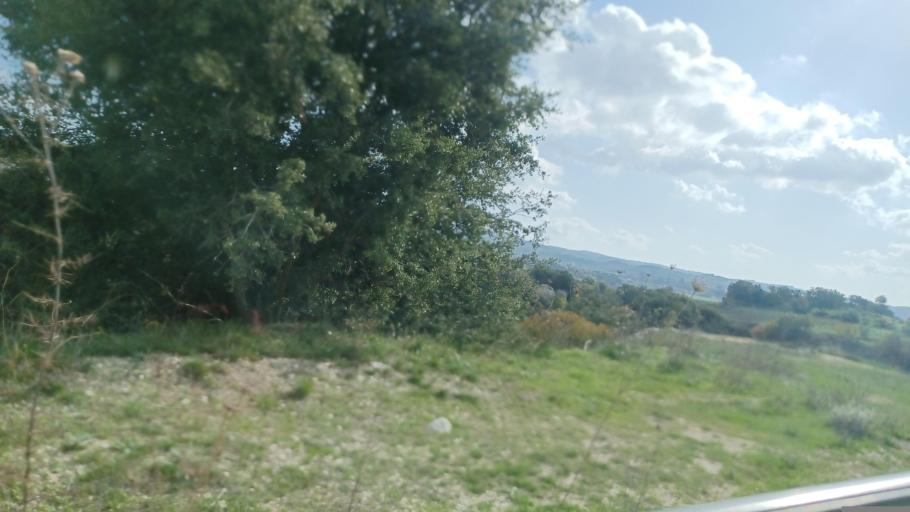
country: CY
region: Pafos
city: Mesogi
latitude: 34.8632
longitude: 32.5373
